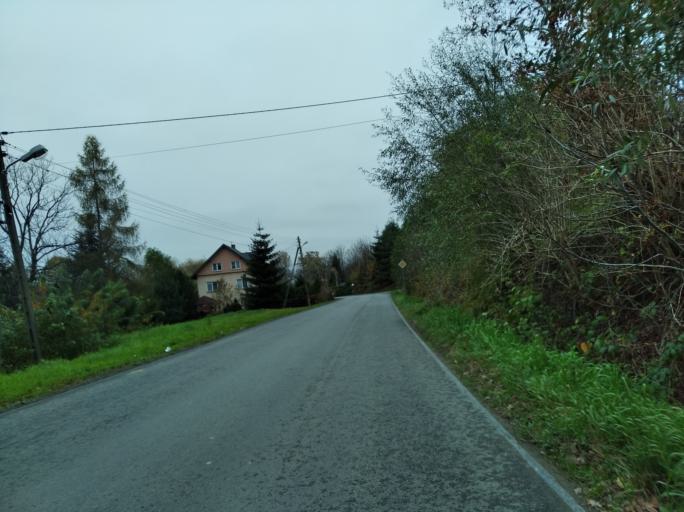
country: PL
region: Subcarpathian Voivodeship
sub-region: Powiat krosnienski
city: Jedlicze
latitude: 49.7342
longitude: 21.6518
